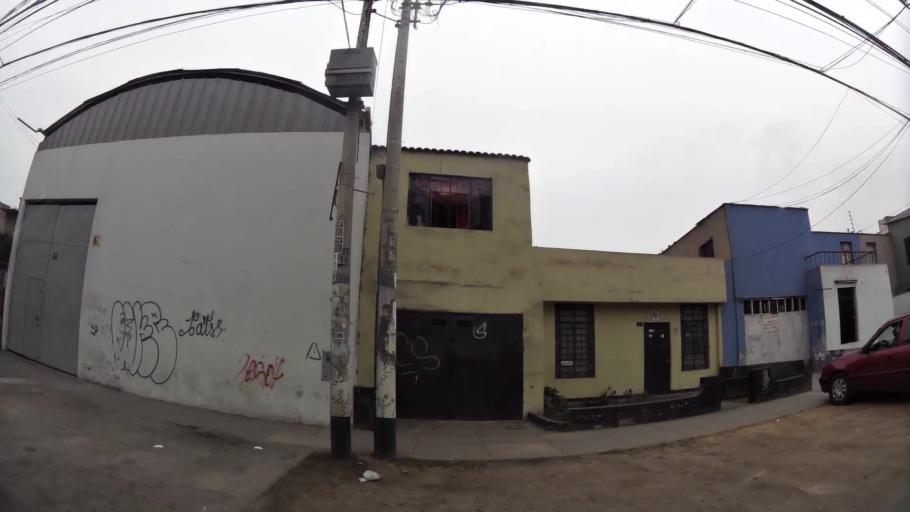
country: PE
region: Lima
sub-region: Lima
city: San Luis
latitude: -12.0762
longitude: -77.0238
